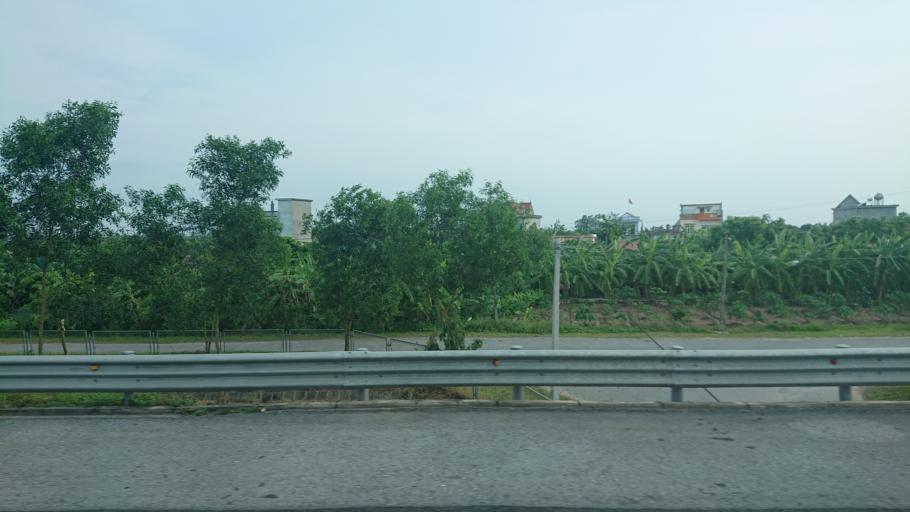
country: VN
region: Hai Phong
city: An Lao
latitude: 20.8130
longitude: 106.4992
